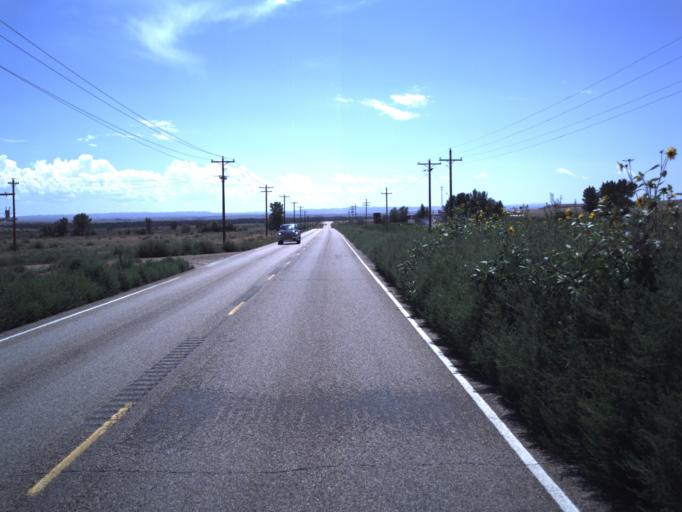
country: US
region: Utah
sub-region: Uintah County
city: Naples
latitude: 40.1439
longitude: -109.6641
